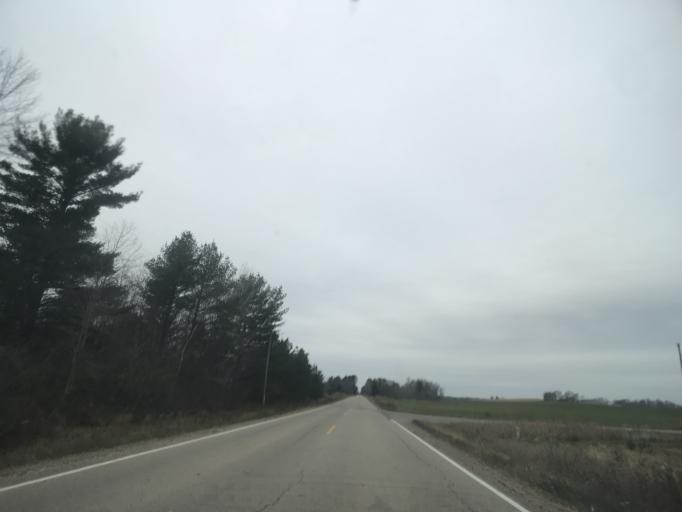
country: US
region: Wisconsin
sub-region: Oconto County
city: Gillett
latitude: 44.9836
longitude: -88.3155
